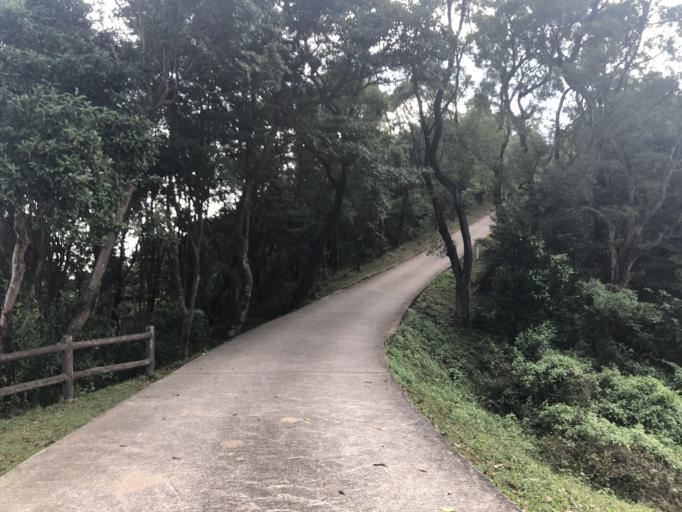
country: HK
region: Tsuen Wan
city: Tsuen Wan
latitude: 22.4023
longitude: 114.0961
